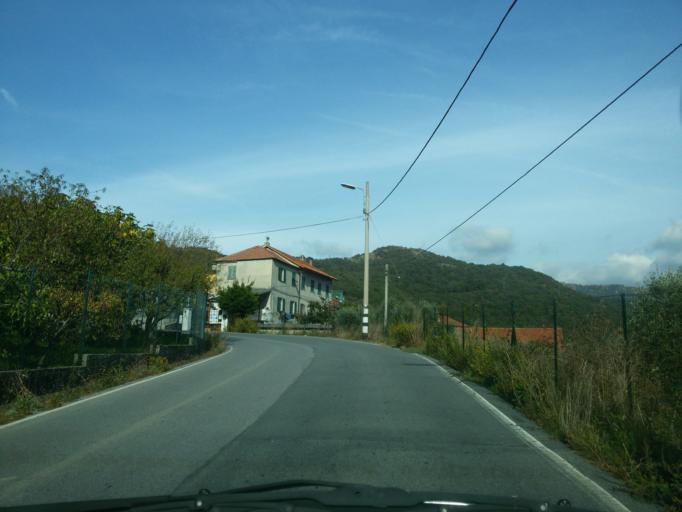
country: IT
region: Liguria
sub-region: Provincia di Genova
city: Piccarello
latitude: 44.4651
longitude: 8.9641
